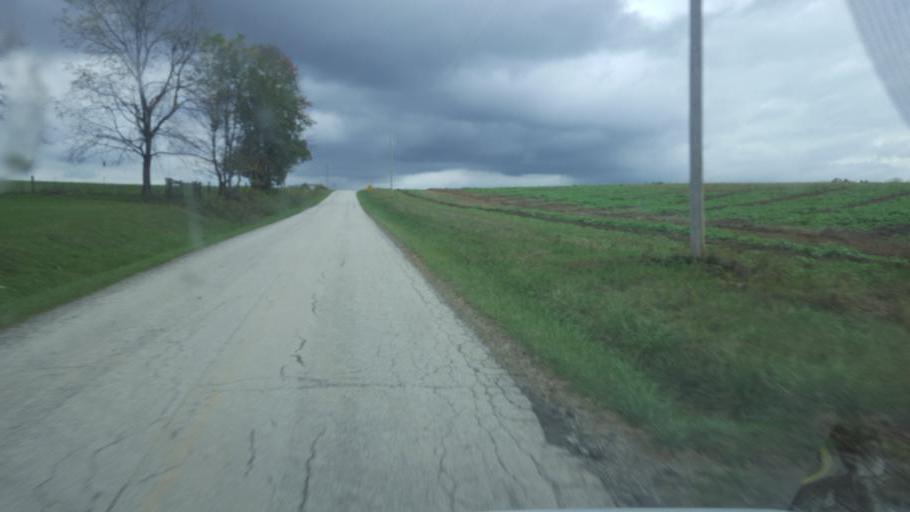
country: US
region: Ohio
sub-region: Ashland County
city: Loudonville
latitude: 40.5623
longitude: -82.1626
